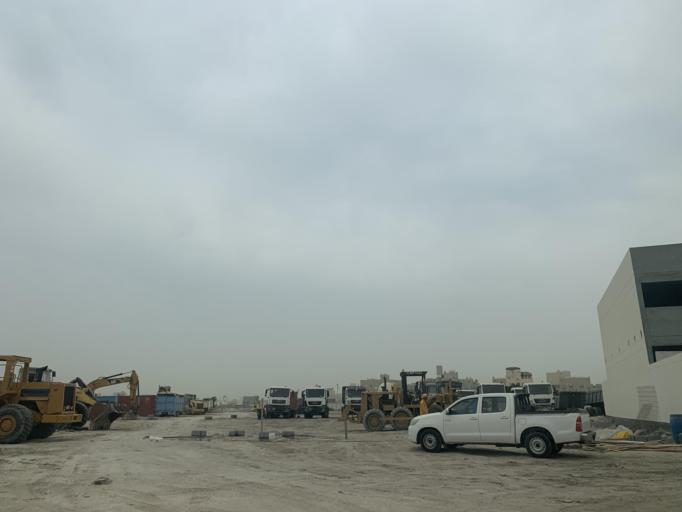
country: BH
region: Northern
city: Madinat `Isa
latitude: 26.1794
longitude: 50.5121
